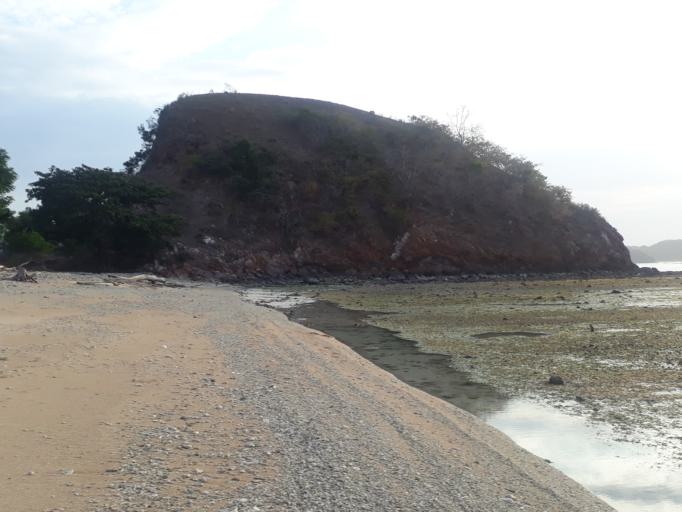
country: ID
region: West Nusa Tenggara
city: Tawun
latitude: -8.7317
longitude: 115.8857
